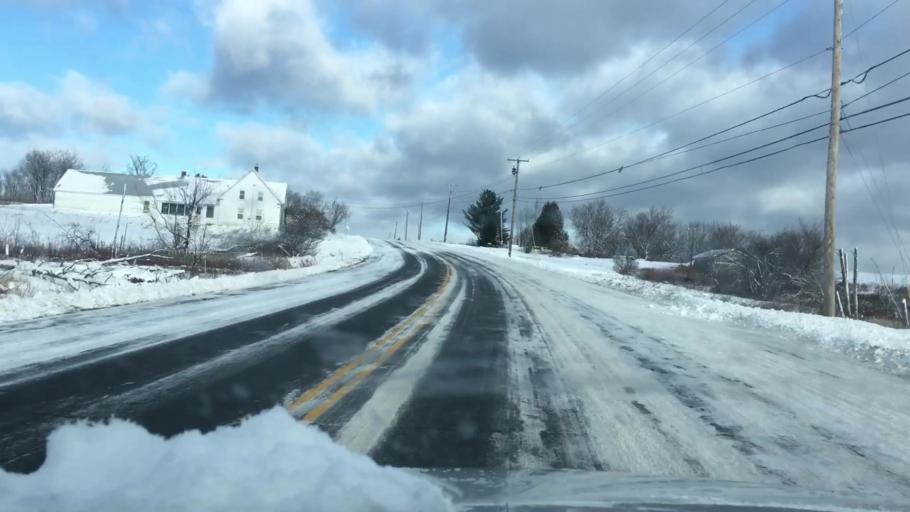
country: US
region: Maine
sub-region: Aroostook County
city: Caribou
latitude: 46.9486
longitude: -68.0231
